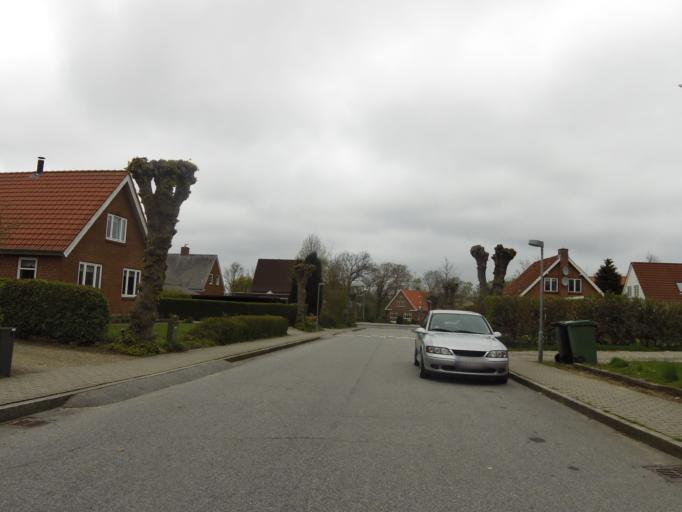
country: DK
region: South Denmark
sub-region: Haderslev Kommune
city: Gram
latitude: 55.2889
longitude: 9.0433
